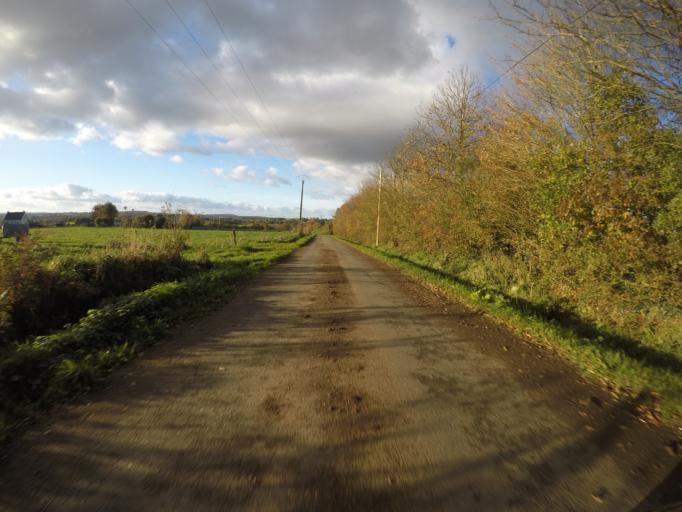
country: FR
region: Brittany
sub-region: Departement des Cotes-d'Armor
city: Louargat
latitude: 48.4698
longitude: -3.2946
